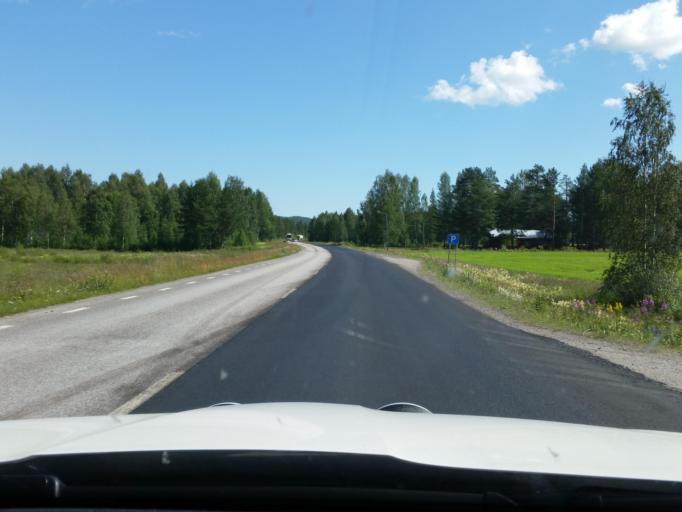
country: SE
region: Norrbotten
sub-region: Alvsbyns Kommun
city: AElvsbyn
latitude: 65.6937
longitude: 20.6604
